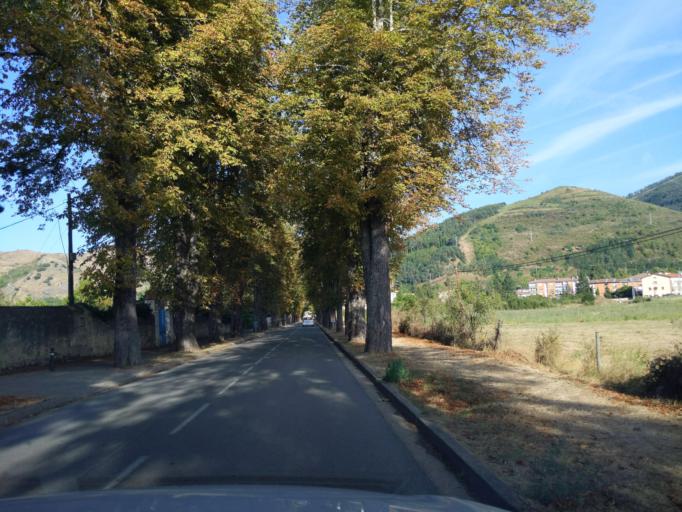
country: ES
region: La Rioja
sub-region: Provincia de La Rioja
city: Ezcaray
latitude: 42.3256
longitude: -3.0206
